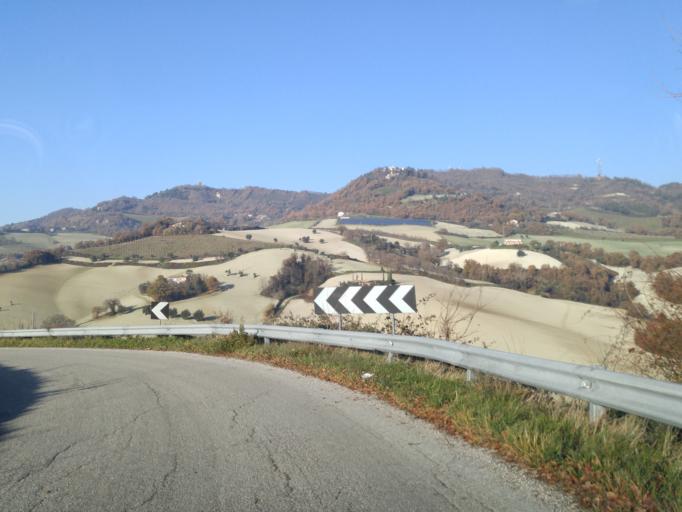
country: IT
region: The Marches
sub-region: Provincia di Pesaro e Urbino
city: Montefelcino
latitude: 43.7509
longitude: 12.8130
